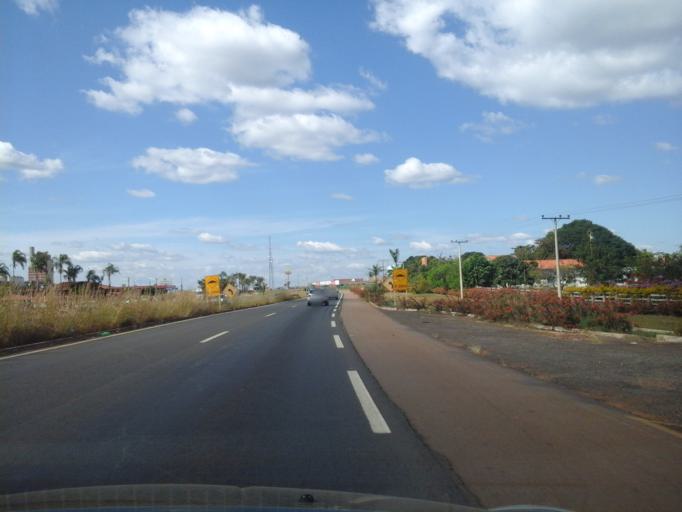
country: BR
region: Goias
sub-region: Abadiania
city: Abadiania
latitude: -16.1206
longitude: -48.4054
